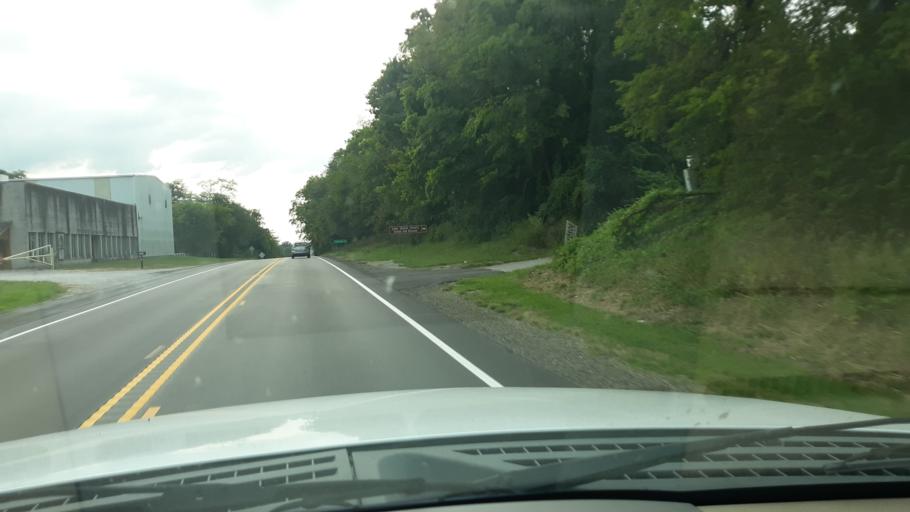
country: US
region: Indiana
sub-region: Gibson County
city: Princeton
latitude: 38.3558
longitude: -87.6554
